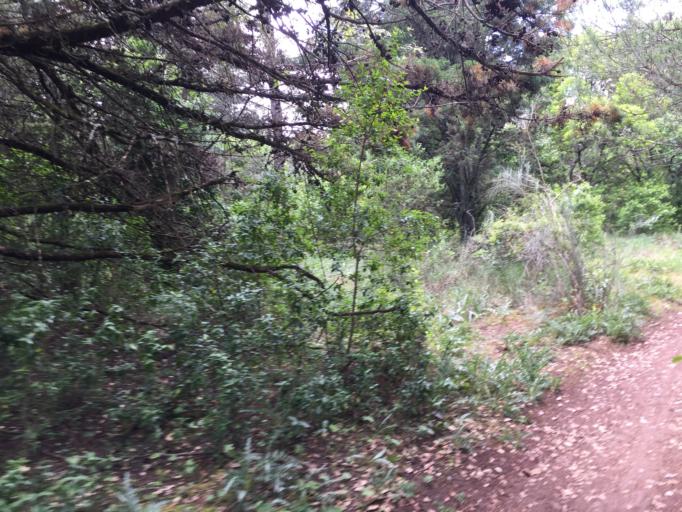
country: PT
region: Lisbon
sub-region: Odivelas
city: Pontinha
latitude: 38.7367
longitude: -9.1899
